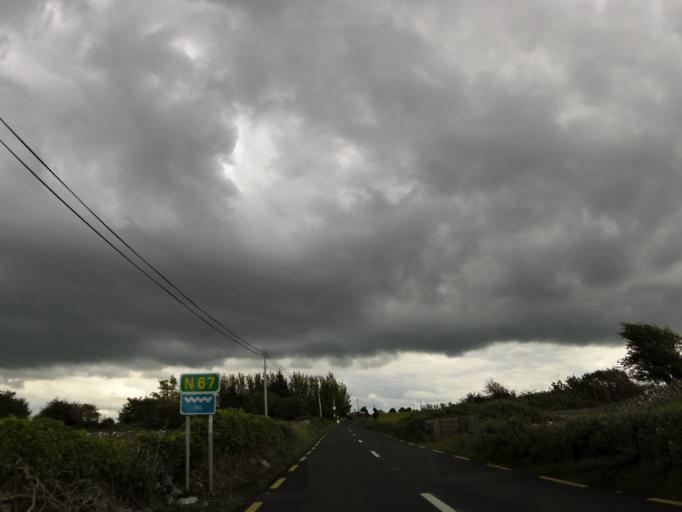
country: IE
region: Connaught
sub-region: County Galway
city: Oranmore
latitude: 53.1433
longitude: -8.9771
